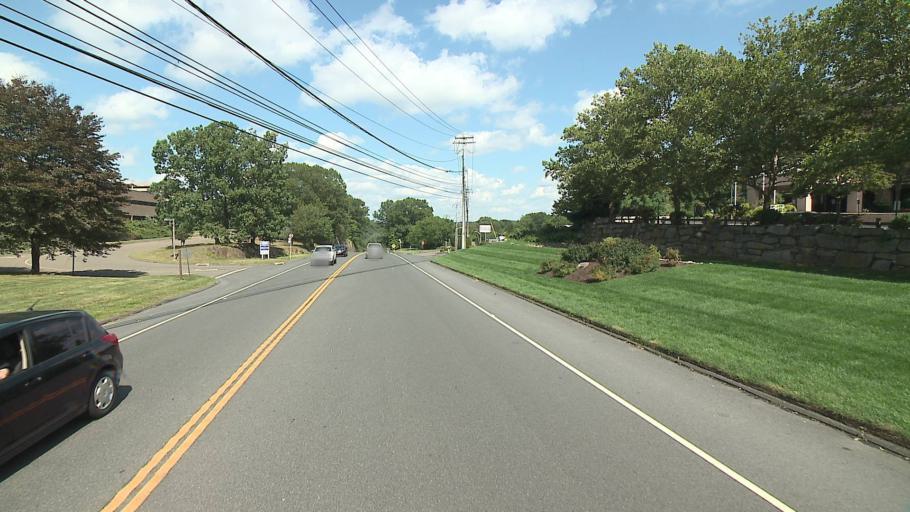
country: US
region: Connecticut
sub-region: Fairfield County
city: Shelton
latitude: 41.2712
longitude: -73.1274
